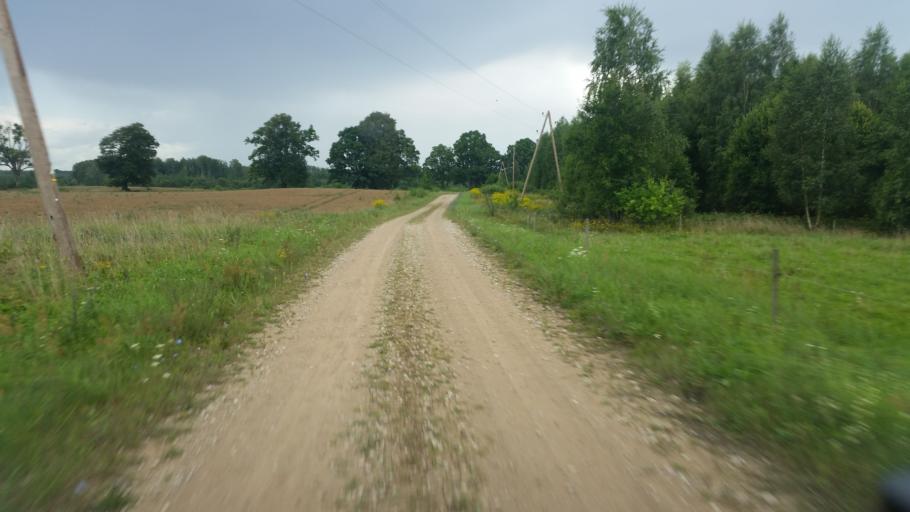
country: LV
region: Vecumnieki
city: Vecumnieki
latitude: 56.4637
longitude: 24.6667
